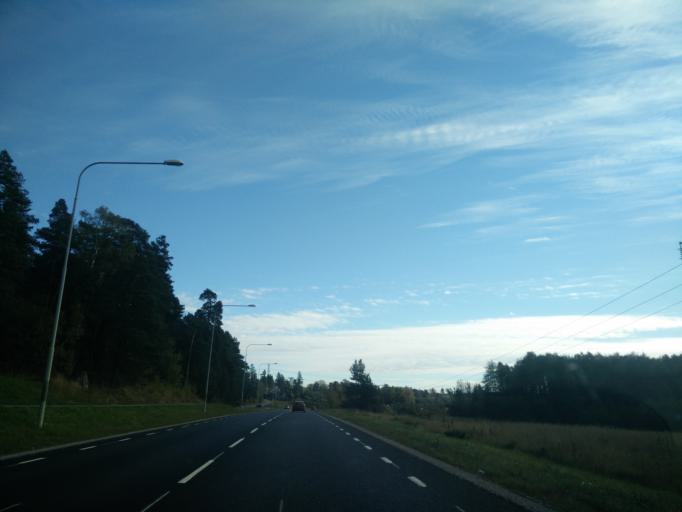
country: SE
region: Stockholm
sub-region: Upplands Vasby Kommun
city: Upplands Vaesby
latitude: 59.5104
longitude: 17.9581
